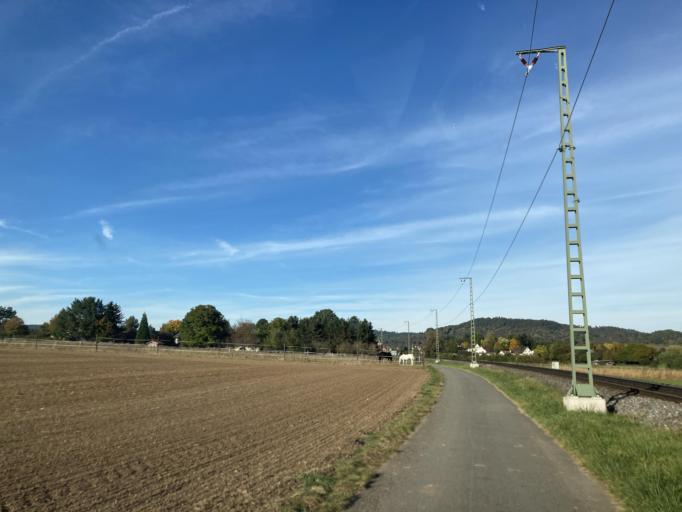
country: DE
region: Baden-Wuerttemberg
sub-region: Tuebingen Region
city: Rottenburg
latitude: 48.5419
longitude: 8.9628
